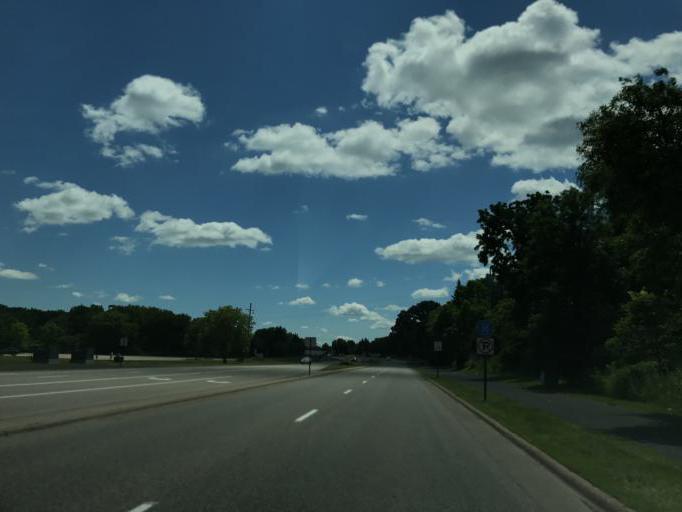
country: US
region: Minnesota
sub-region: Hennepin County
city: Maple Grove
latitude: 45.0811
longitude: -93.4778
